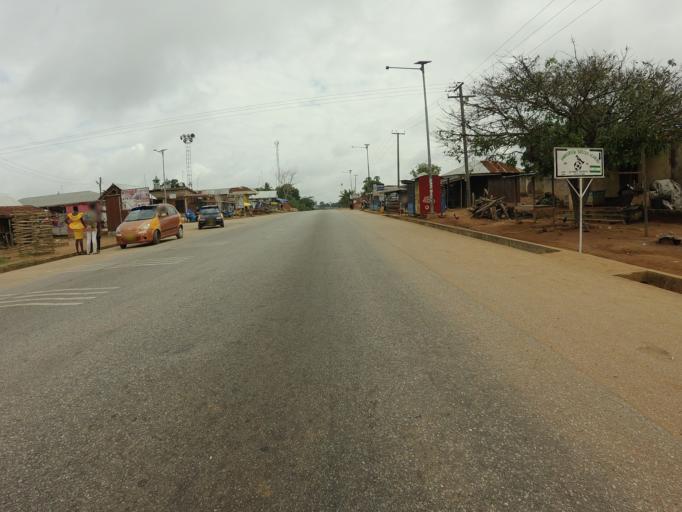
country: GH
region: Ashanti
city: Tafo
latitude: 6.9682
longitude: -1.6818
